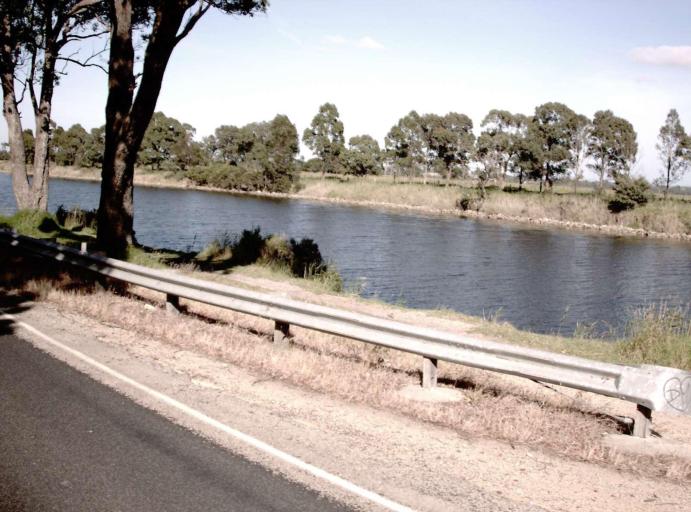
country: AU
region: Victoria
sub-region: East Gippsland
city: Lakes Entrance
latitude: -37.8419
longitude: 147.8573
